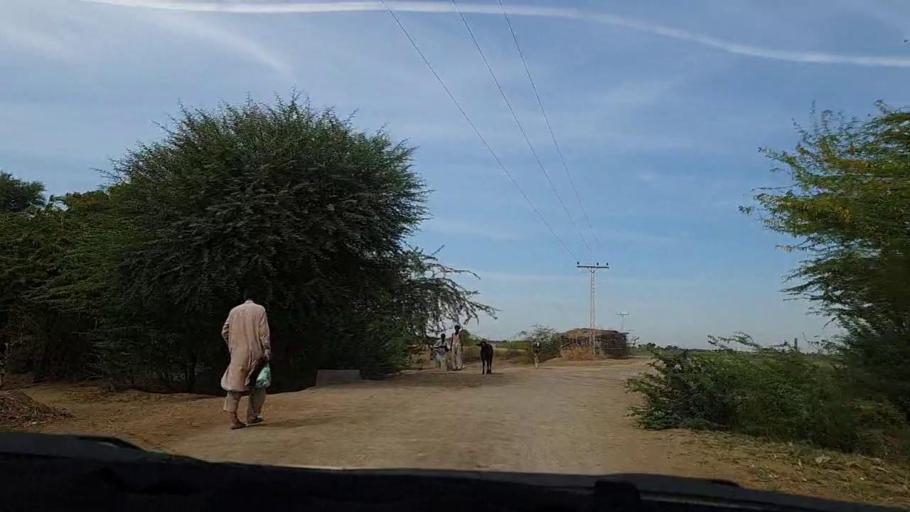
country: PK
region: Sindh
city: Dhoro Naro
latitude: 25.4784
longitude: 69.4789
